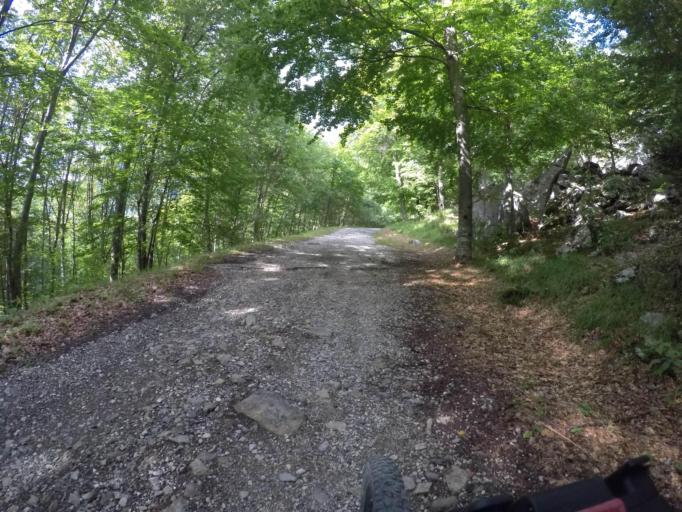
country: IT
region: Friuli Venezia Giulia
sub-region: Provincia di Udine
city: Paularo
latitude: 46.4865
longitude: 13.1825
